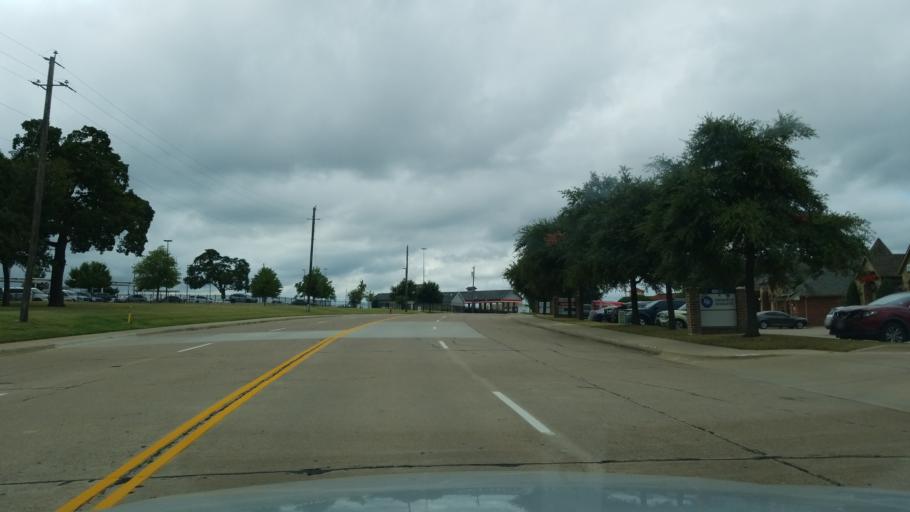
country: US
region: Texas
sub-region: Tarrant County
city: Bedford
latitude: 32.8433
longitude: -97.1201
